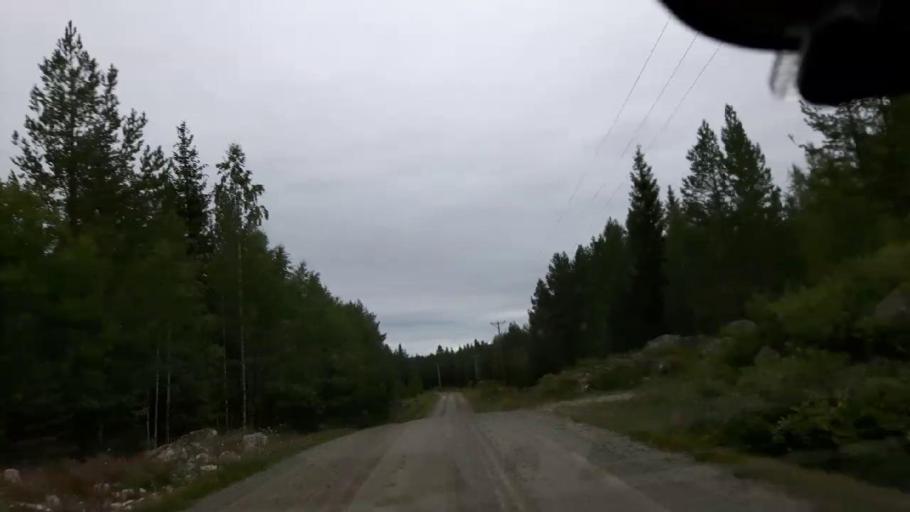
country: SE
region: Vaesternorrland
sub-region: Ange Kommun
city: Fransta
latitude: 62.8076
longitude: 16.0188
